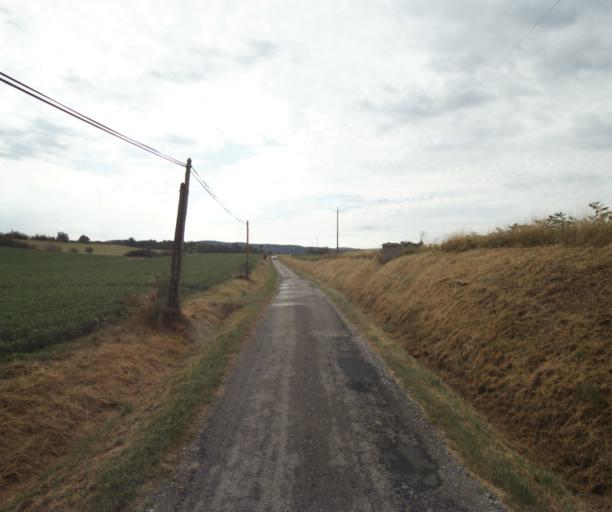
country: FR
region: Midi-Pyrenees
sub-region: Departement de la Haute-Garonne
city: Revel
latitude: 43.4331
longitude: 1.9728
